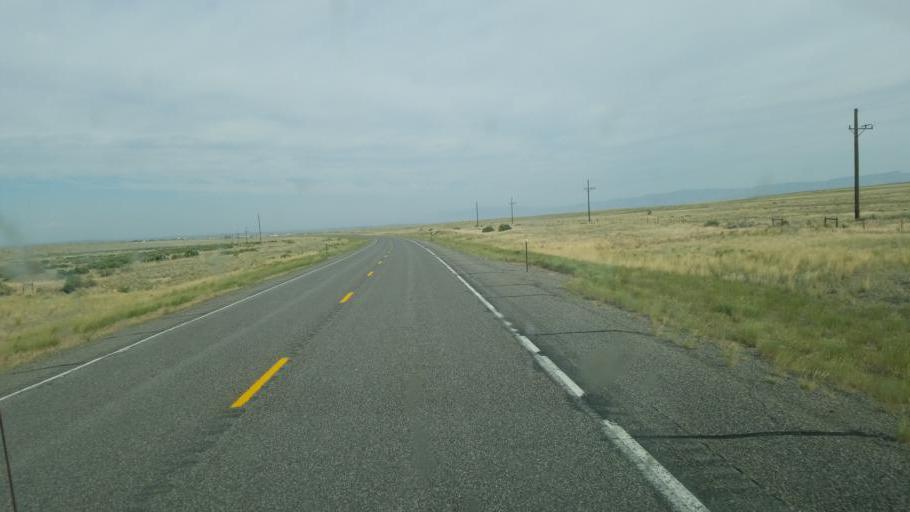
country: US
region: Wyoming
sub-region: Fremont County
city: Riverton
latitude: 43.2319
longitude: -108.0635
